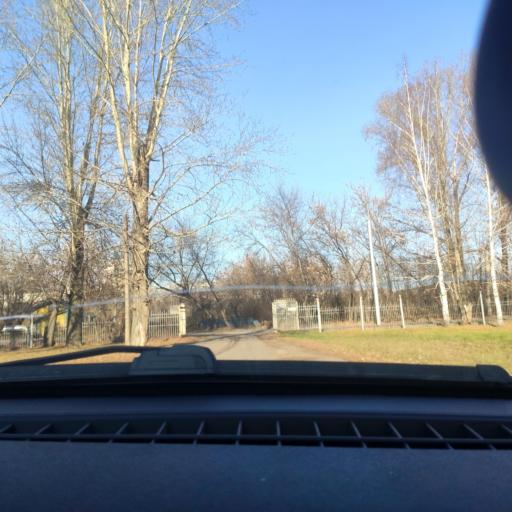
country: RU
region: Bashkortostan
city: Ufa
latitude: 54.7992
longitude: 56.1348
